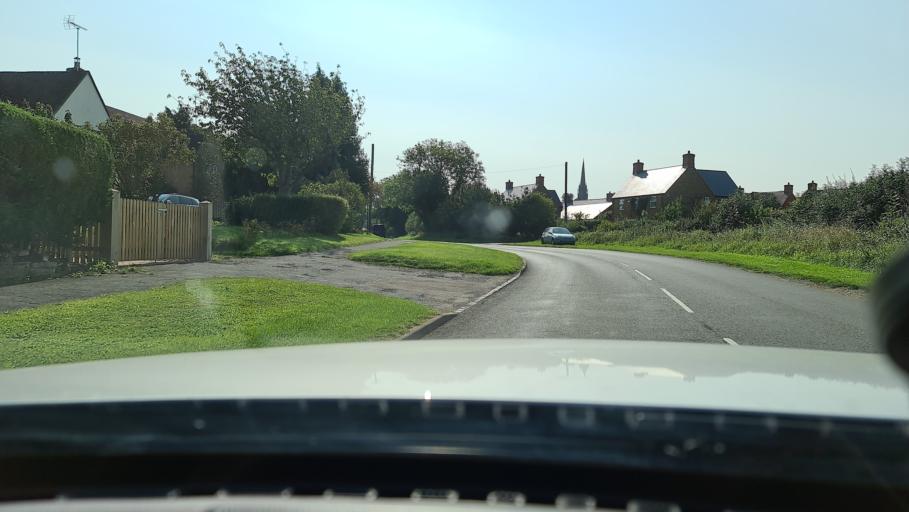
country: GB
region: England
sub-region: Oxfordshire
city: Adderbury
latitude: 52.0259
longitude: -1.2789
